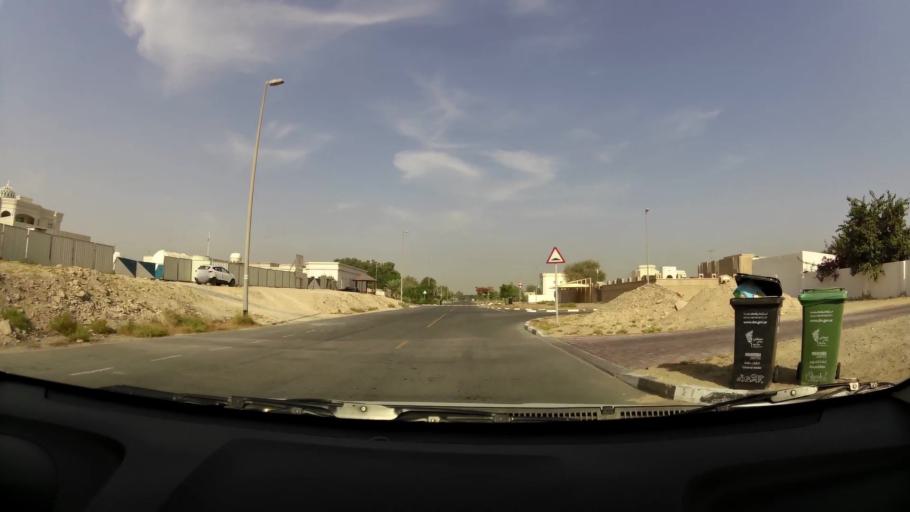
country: AE
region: Ash Shariqah
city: Sharjah
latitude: 25.2458
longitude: 55.4114
